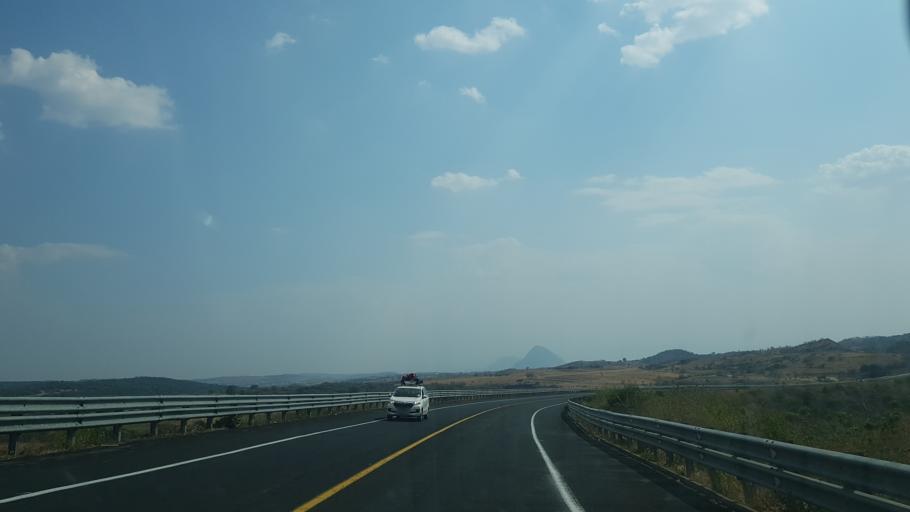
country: MX
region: Puebla
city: San Juan Amecac
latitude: 18.8148
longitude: -98.6960
